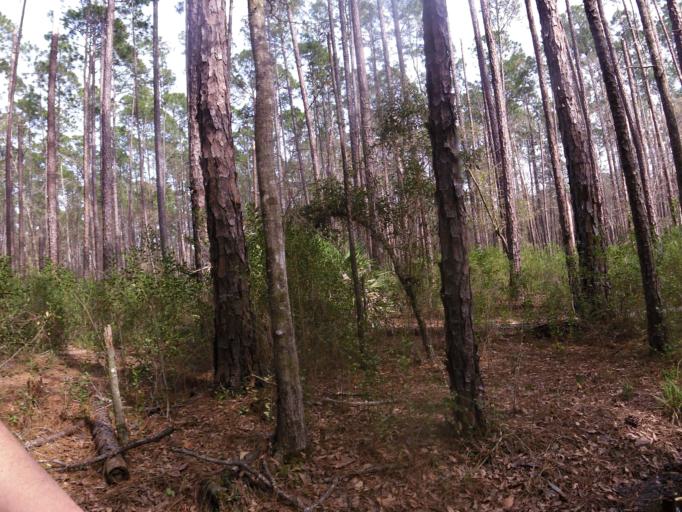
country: US
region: Florida
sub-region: Clay County
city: Middleburg
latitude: 30.1233
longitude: -81.9086
